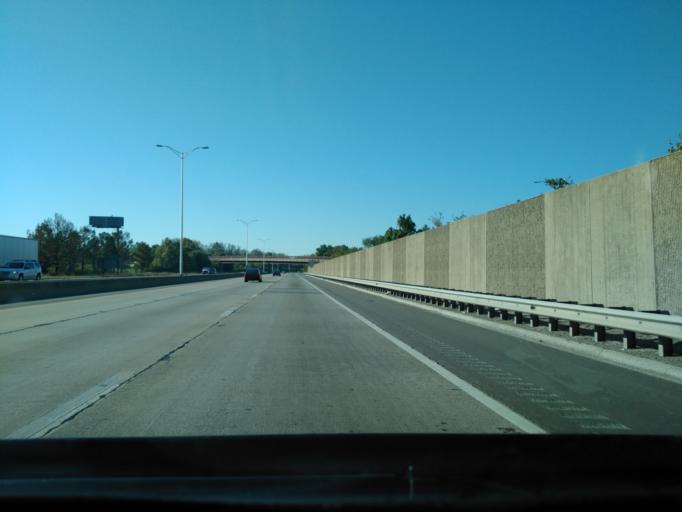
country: US
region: Illinois
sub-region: Saint Clair County
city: Alorton
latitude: 38.5985
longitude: -90.0880
